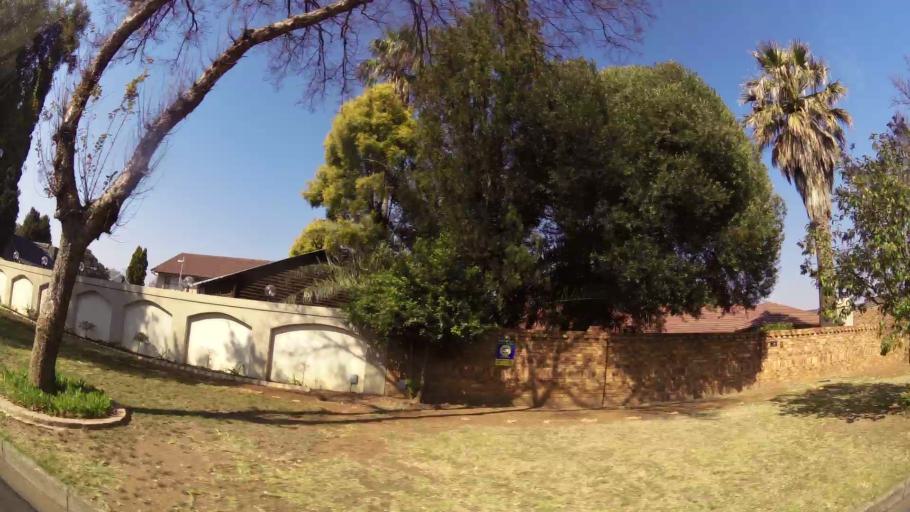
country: ZA
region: Gauteng
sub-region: Ekurhuleni Metropolitan Municipality
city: Boksburg
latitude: -26.2488
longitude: 28.2668
